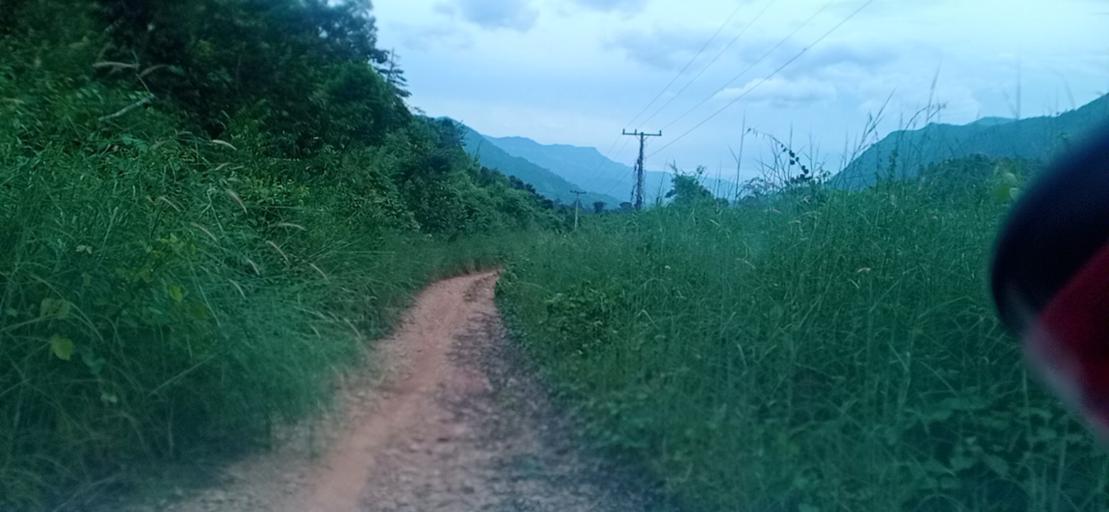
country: TH
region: Changwat Bueng Kan
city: Pak Khat
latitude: 18.5628
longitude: 103.2737
